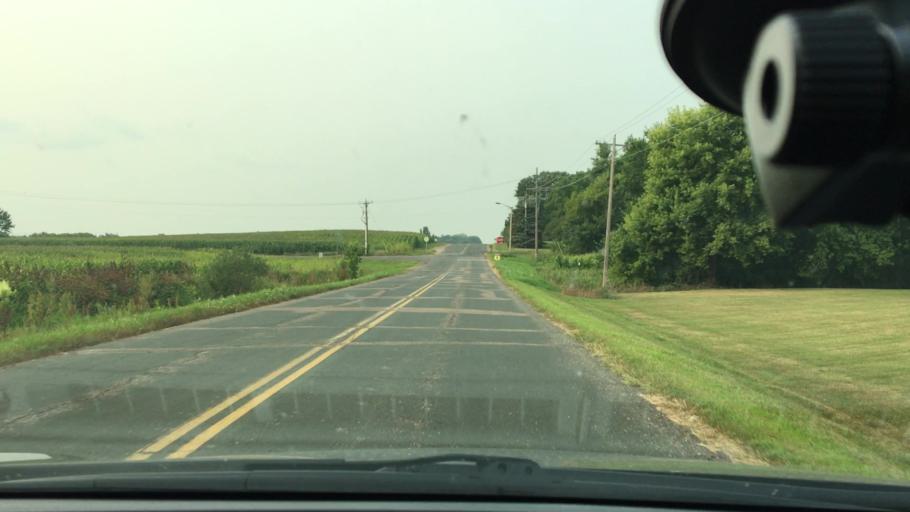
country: US
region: Minnesota
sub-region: Wright County
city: Albertville
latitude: 45.2727
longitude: -93.6841
